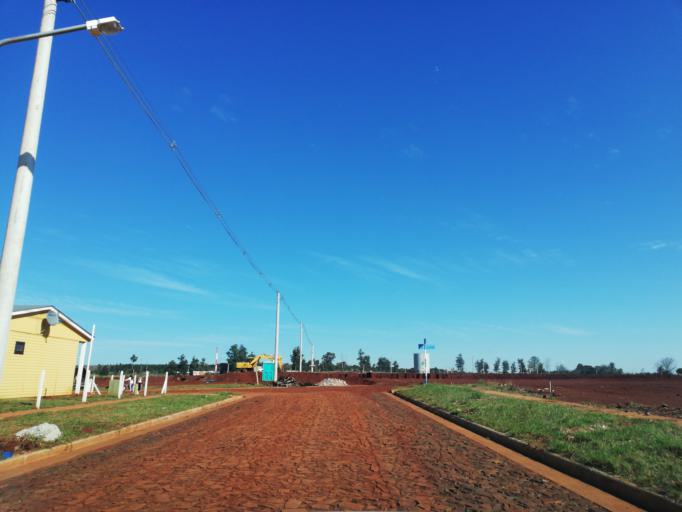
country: AR
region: Misiones
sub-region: Departamento de Capital
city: Posadas
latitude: -27.4154
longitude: -55.9919
